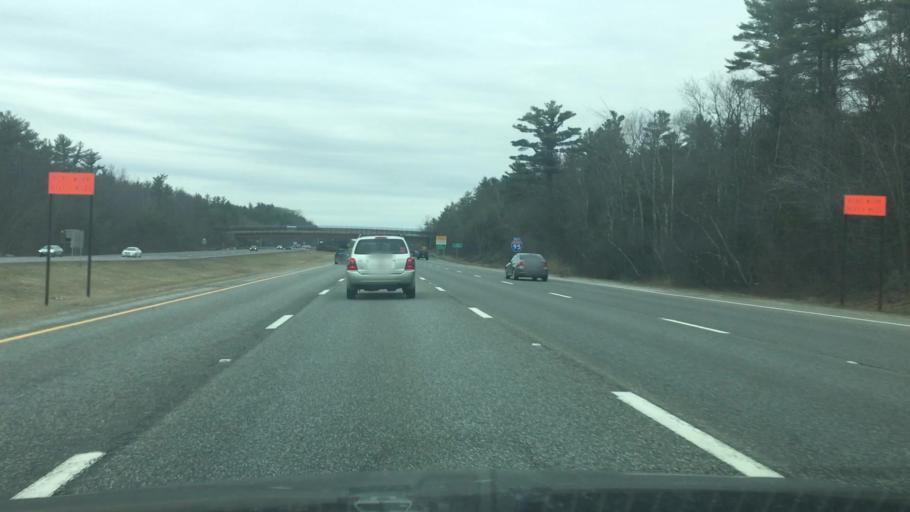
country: US
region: Massachusetts
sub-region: Essex County
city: Boxford
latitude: 42.6998
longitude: -70.9676
